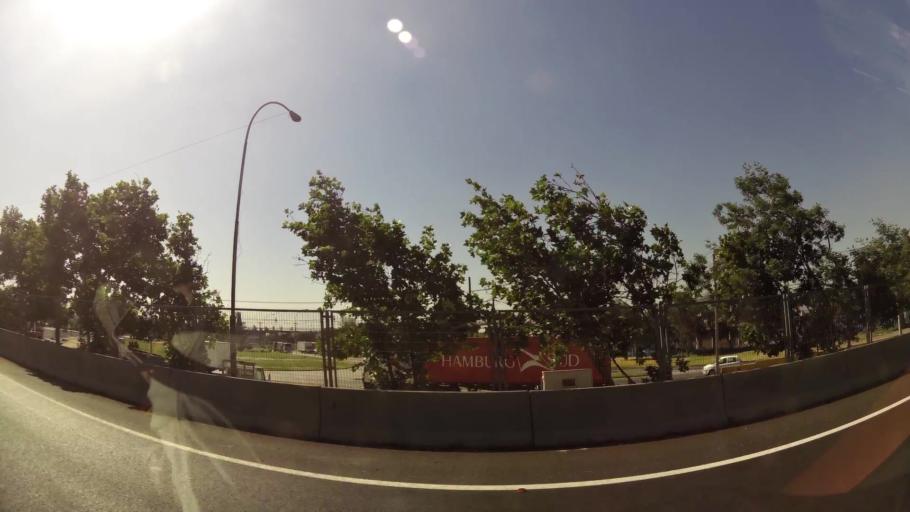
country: CL
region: Santiago Metropolitan
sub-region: Provincia de Maipo
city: San Bernardo
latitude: -33.5513
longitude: -70.7026
